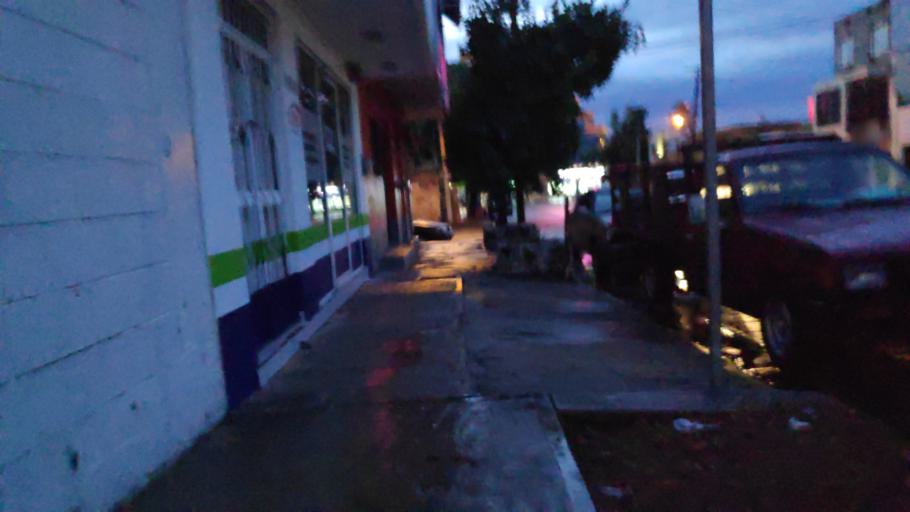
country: MX
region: Sinaloa
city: Culiacan
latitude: 24.8032
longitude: -107.4035
